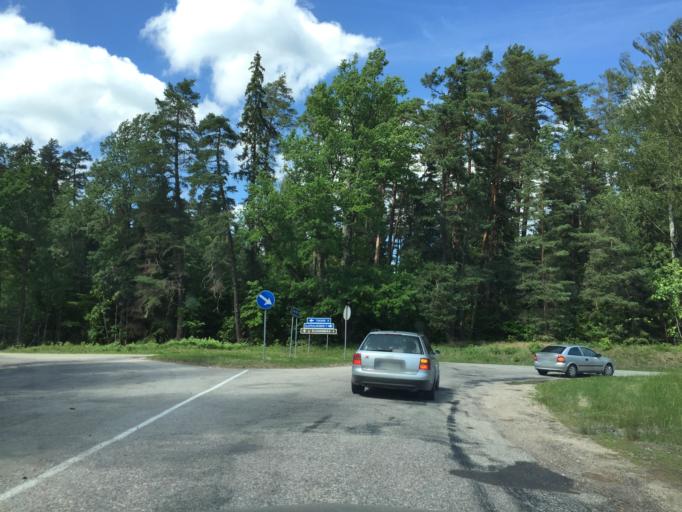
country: LV
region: Engure
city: Smarde
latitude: 56.9838
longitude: 23.2797
